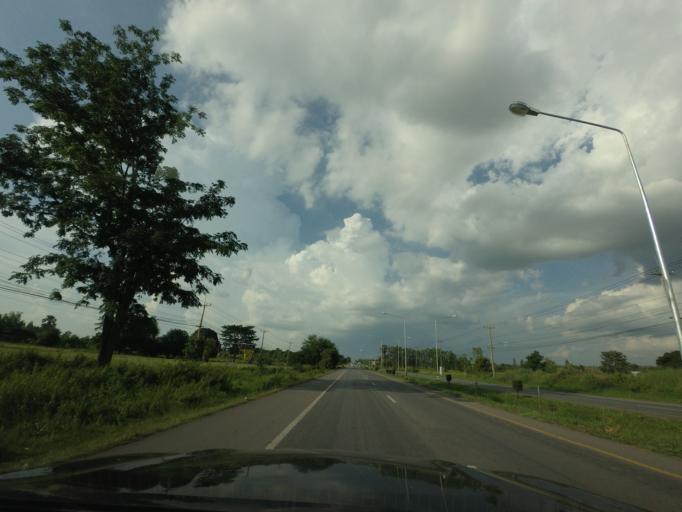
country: TH
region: Khon Kaen
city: Ban Haet
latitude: 16.2359
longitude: 102.7684
